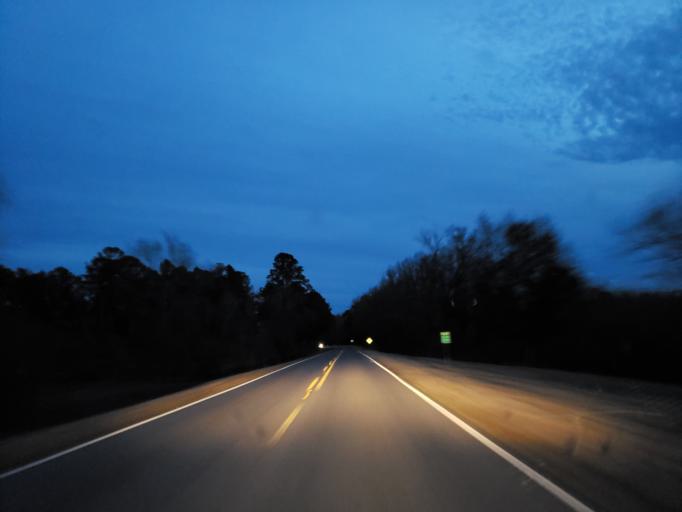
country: US
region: Alabama
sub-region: Greene County
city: Eutaw
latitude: 32.8738
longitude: -87.9286
